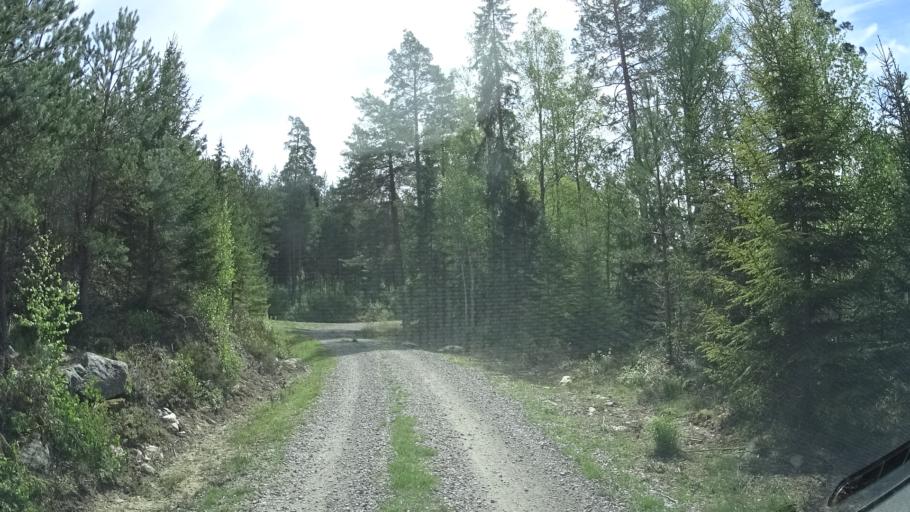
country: SE
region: OEstergoetland
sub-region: Finspangs Kommun
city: Finspang
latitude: 58.8075
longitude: 15.8369
